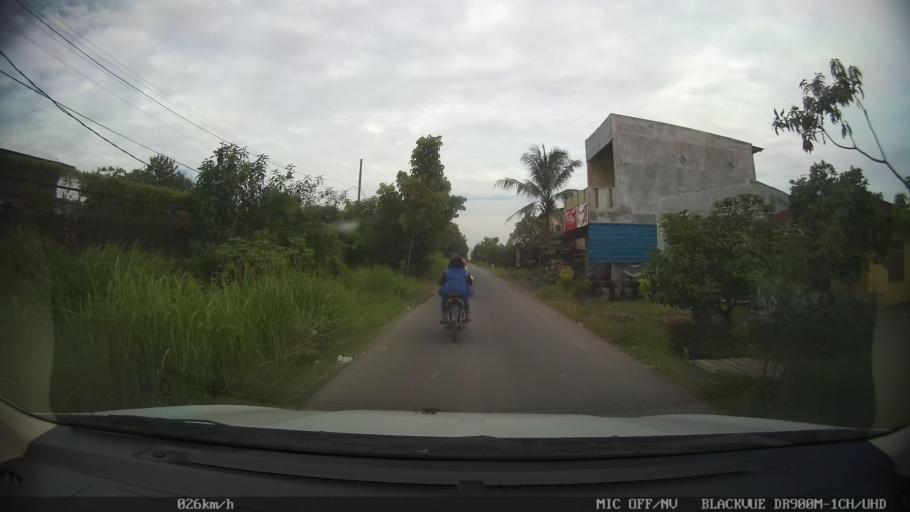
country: ID
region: North Sumatra
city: Sunggal
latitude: 3.6170
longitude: 98.5805
